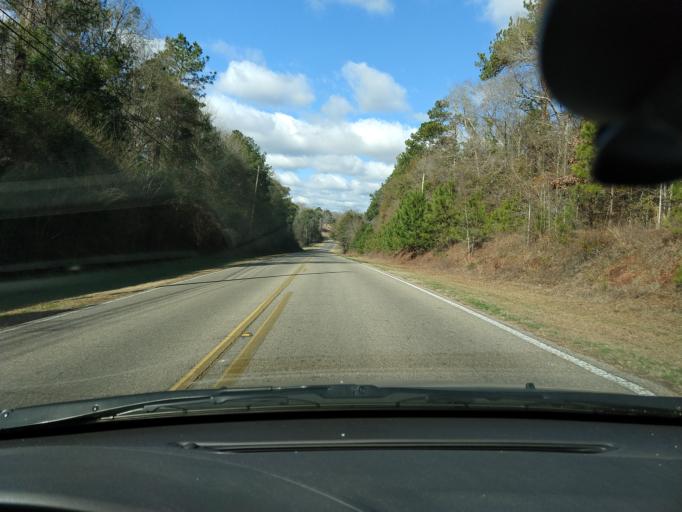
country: US
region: Alabama
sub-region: Coffee County
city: Enterprise
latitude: 31.3211
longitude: -85.8753
